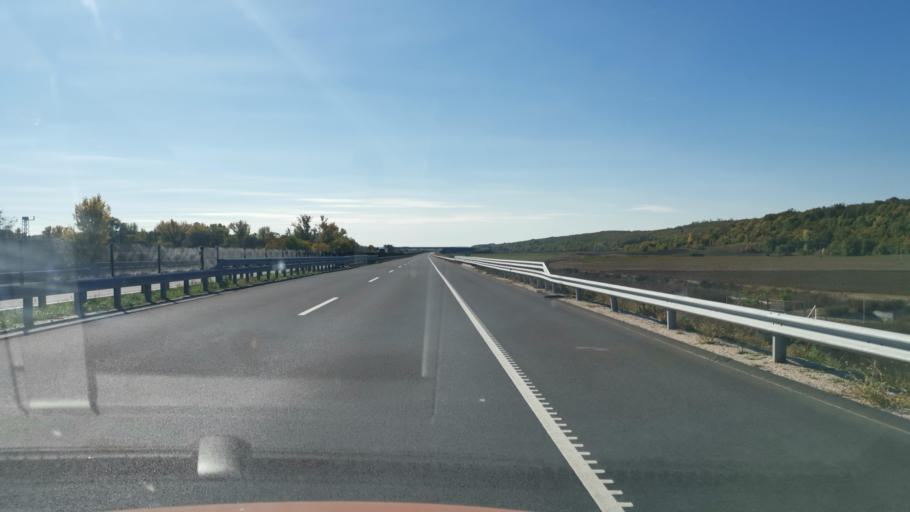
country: HU
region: Borsod-Abauj-Zemplen
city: Gonc
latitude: 48.4575
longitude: 21.1969
